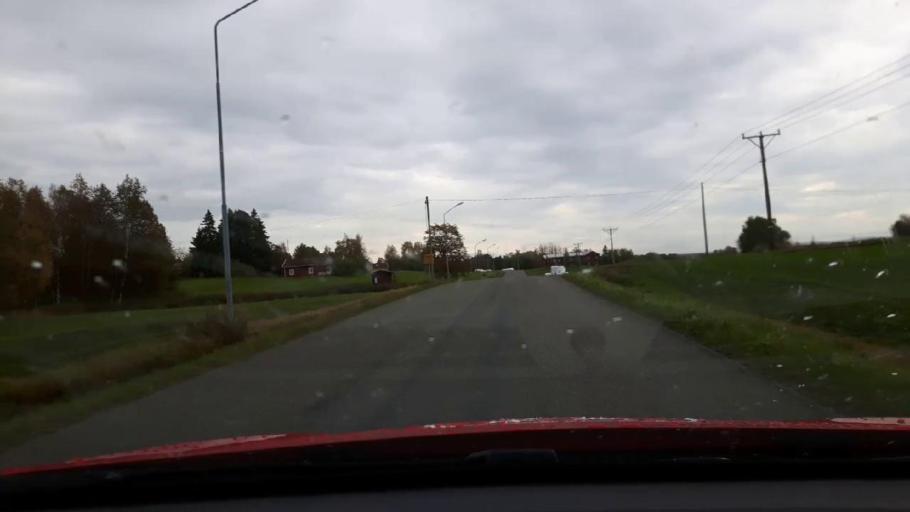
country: SE
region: Jaemtland
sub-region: Bergs Kommun
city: Hoverberg
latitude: 62.9441
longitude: 14.4958
